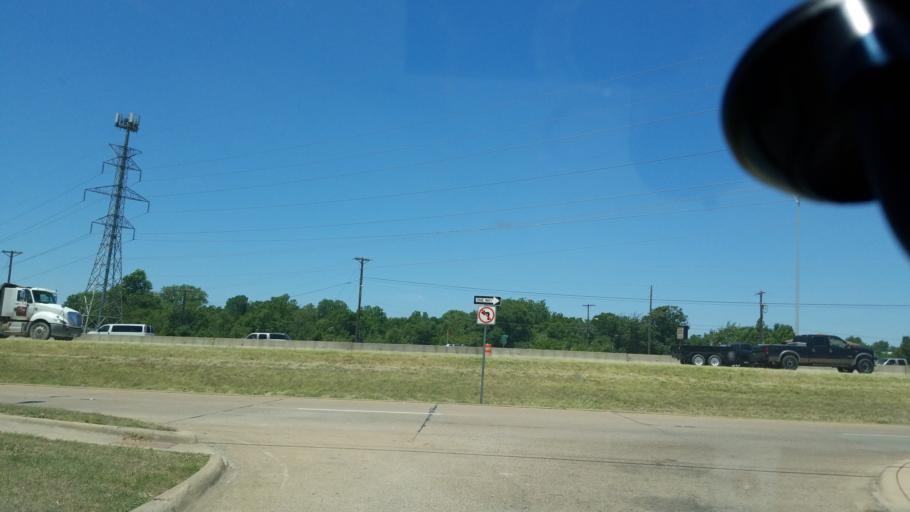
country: US
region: Texas
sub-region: Dallas County
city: Cockrell Hill
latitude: 32.7010
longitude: -96.8352
